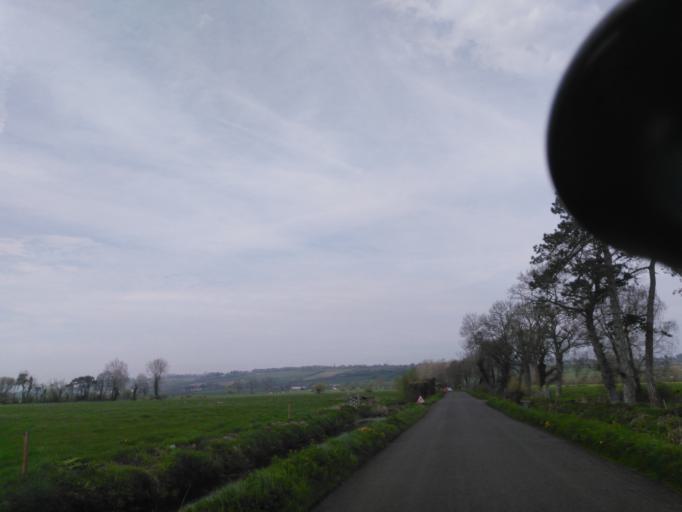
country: GB
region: England
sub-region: Somerset
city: Langport
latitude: 51.1145
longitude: -2.8229
